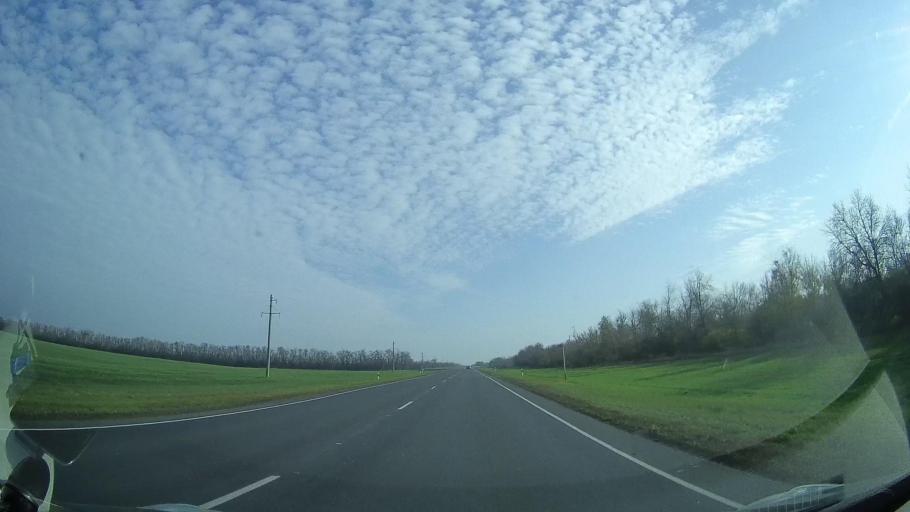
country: RU
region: Rostov
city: Gigant
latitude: 46.5274
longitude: 41.2120
